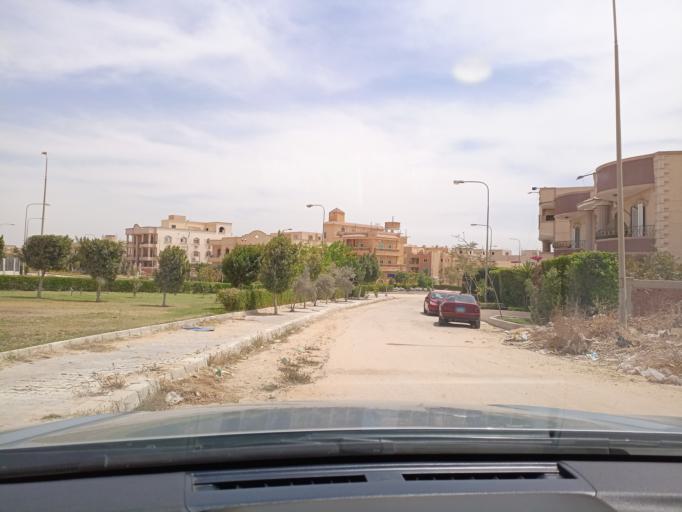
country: EG
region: Muhafazat al Qalyubiyah
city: Al Khankah
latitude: 30.2287
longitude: 31.4886
